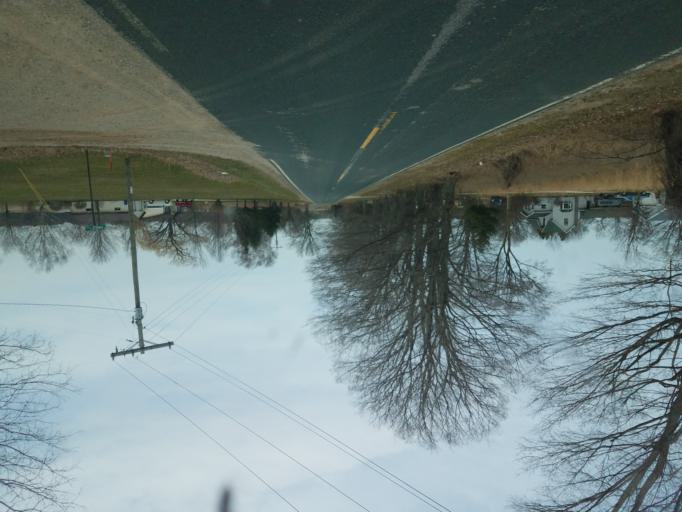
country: US
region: Michigan
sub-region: Oceana County
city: Hart
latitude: 43.7070
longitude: -86.4835
